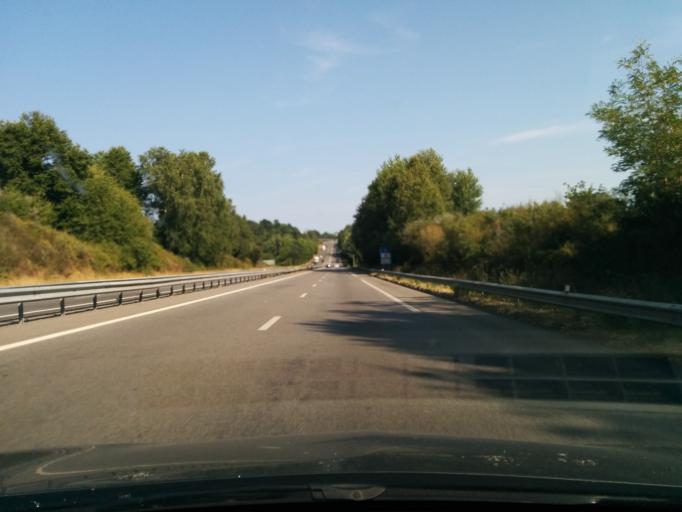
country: FR
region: Limousin
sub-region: Departement de la Haute-Vienne
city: Boisseuil
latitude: 45.7716
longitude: 1.3140
